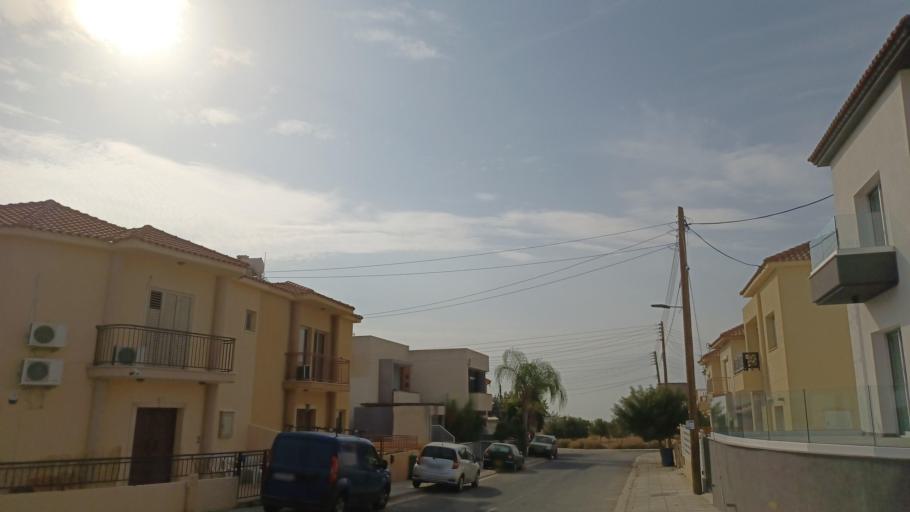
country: CY
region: Limassol
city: Ypsonas
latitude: 34.6954
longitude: 32.9438
